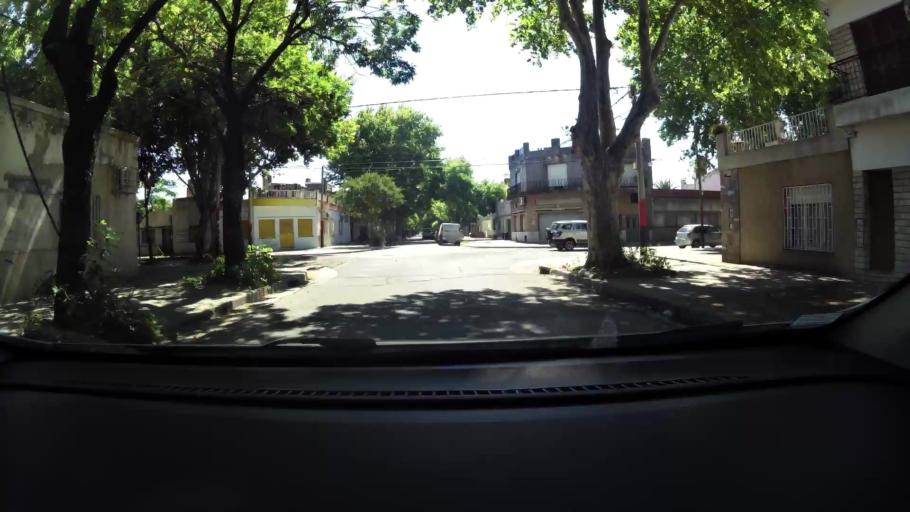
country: AR
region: Santa Fe
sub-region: Departamento de Rosario
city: Rosario
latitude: -32.9469
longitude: -60.6852
